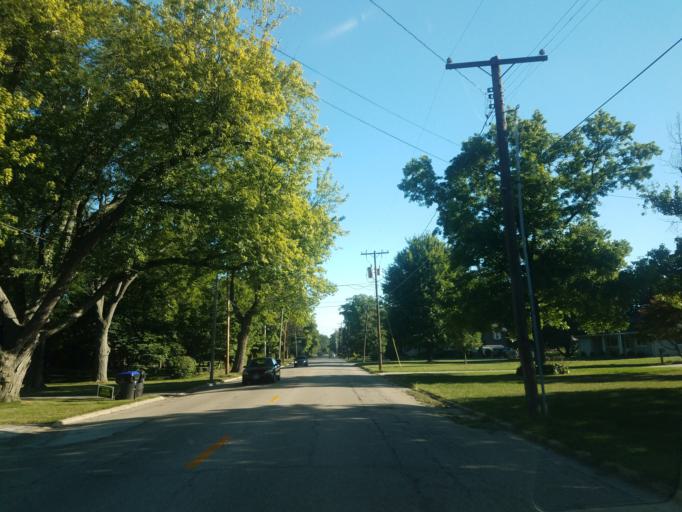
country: US
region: Illinois
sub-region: McLean County
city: Bloomington
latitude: 40.4703
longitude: -88.9627
